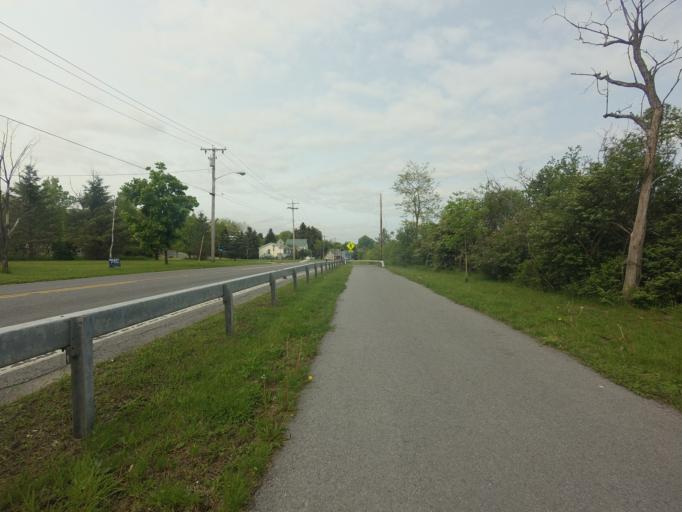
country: US
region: New York
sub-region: Jefferson County
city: Watertown
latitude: 43.9775
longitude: -75.8851
